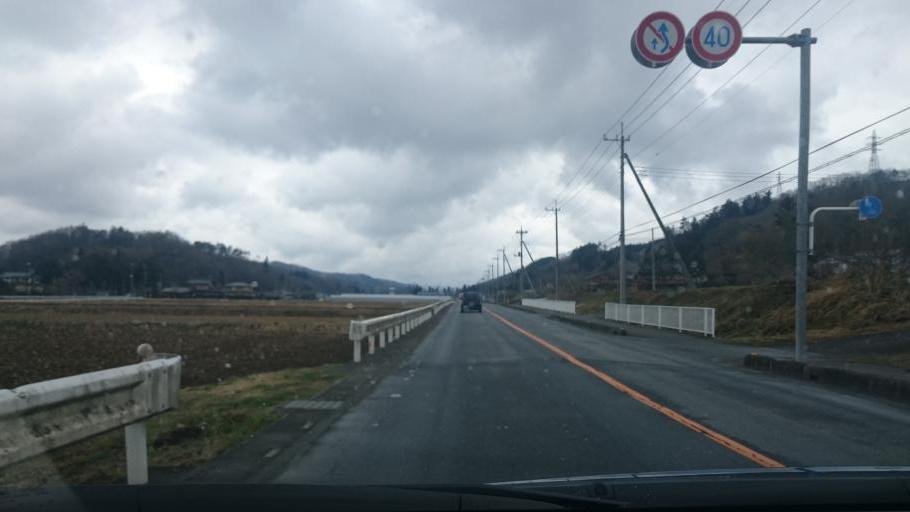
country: JP
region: Saitama
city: Chichibu
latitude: 36.0350
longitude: 139.0782
